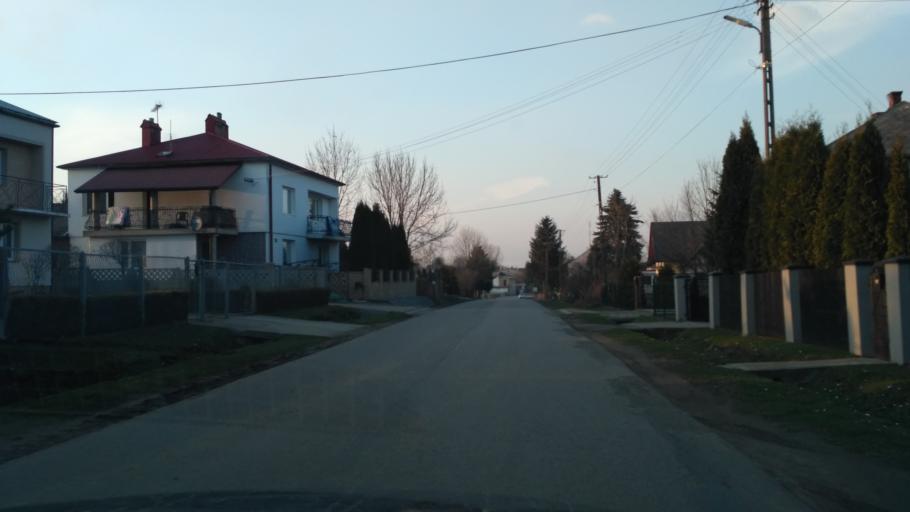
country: PL
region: Subcarpathian Voivodeship
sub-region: Powiat przeworski
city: Zarzecze
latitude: 49.9514
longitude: 22.5571
